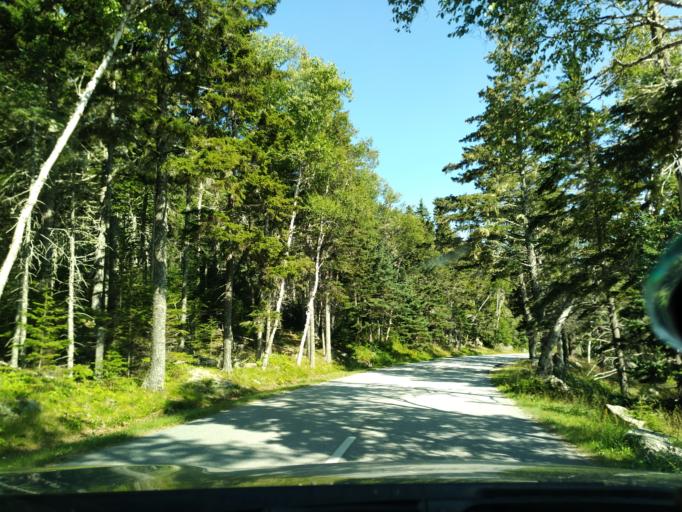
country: US
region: Maine
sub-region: Hancock County
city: Gouldsboro
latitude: 44.3455
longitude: -68.0456
